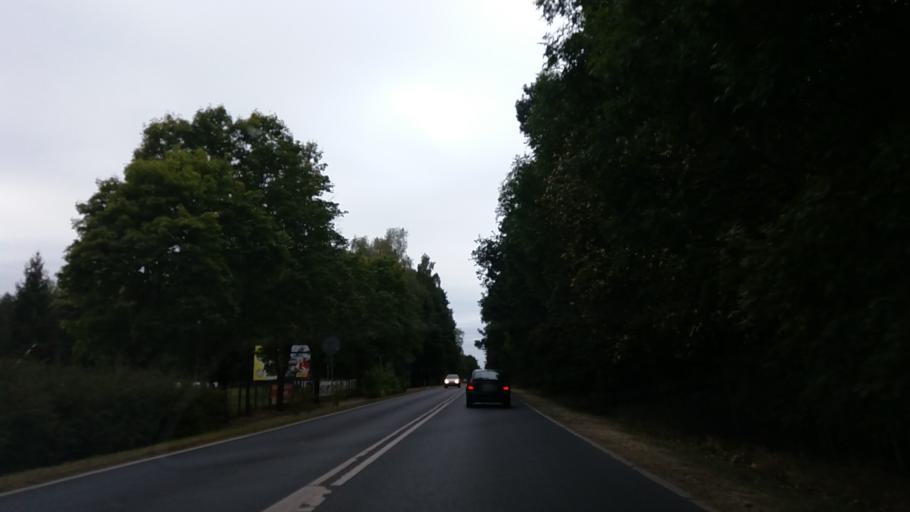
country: PL
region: Lubusz
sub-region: Powiat gorzowski
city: Klodawa
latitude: 52.7716
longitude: 15.2295
